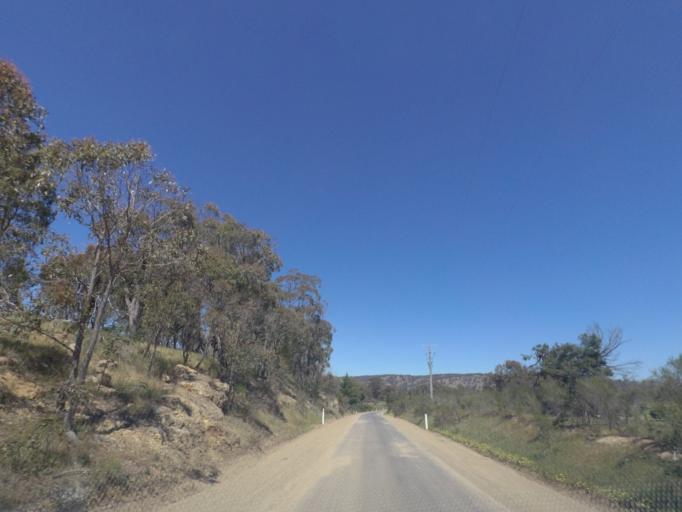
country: AU
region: Victoria
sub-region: Whittlesea
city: Whittlesea
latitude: -37.2867
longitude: 144.9978
